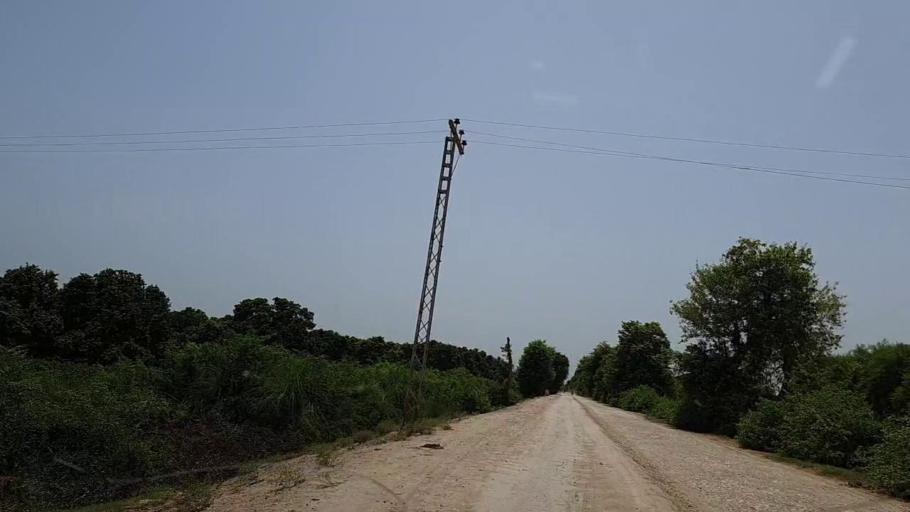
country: PK
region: Sindh
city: Tharu Shah
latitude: 27.0063
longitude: 68.1243
